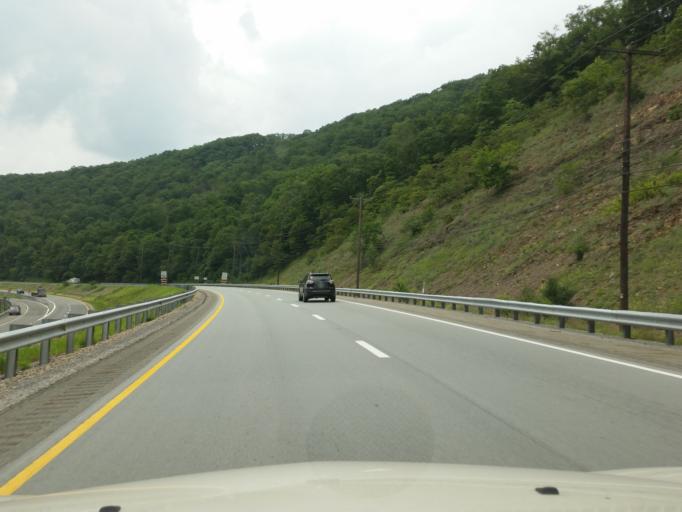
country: US
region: Pennsylvania
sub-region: Perry County
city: Newport
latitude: 40.5642
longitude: -77.1690
